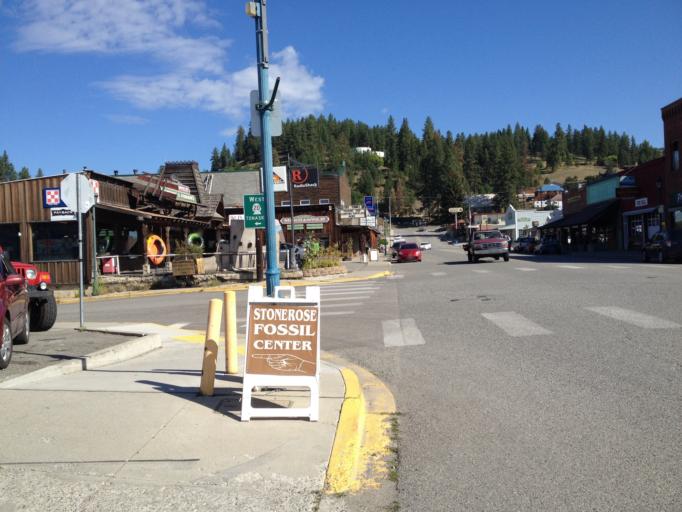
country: US
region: Washington
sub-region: Ferry County
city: Republic
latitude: 48.6476
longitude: -118.7381
